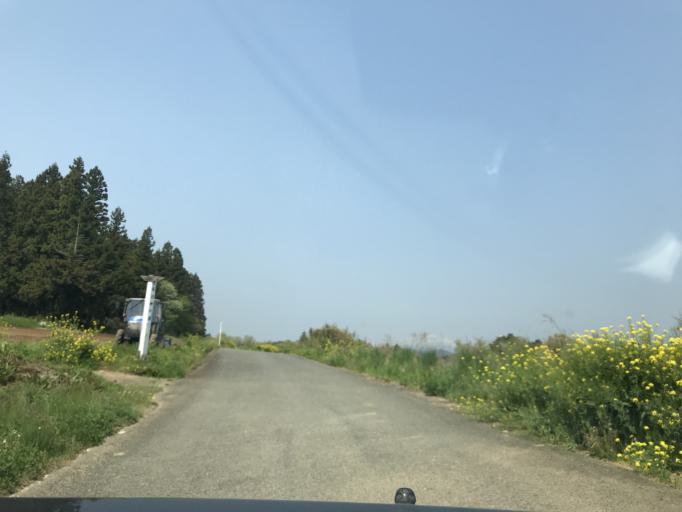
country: JP
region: Iwate
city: Ichinoseki
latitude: 38.8586
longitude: 141.0591
